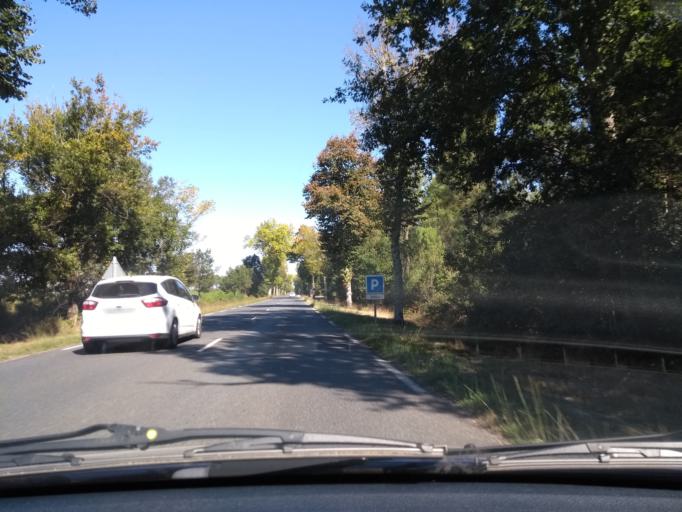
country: FR
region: Aquitaine
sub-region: Departement de la Gironde
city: Belin-Beliet
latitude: 44.5504
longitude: -0.7867
